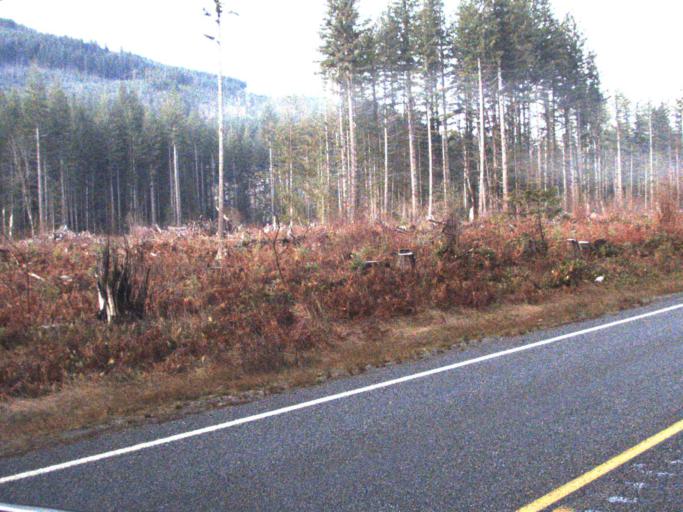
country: US
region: Washington
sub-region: Snohomish County
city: Darrington
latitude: 48.2856
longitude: -121.5726
